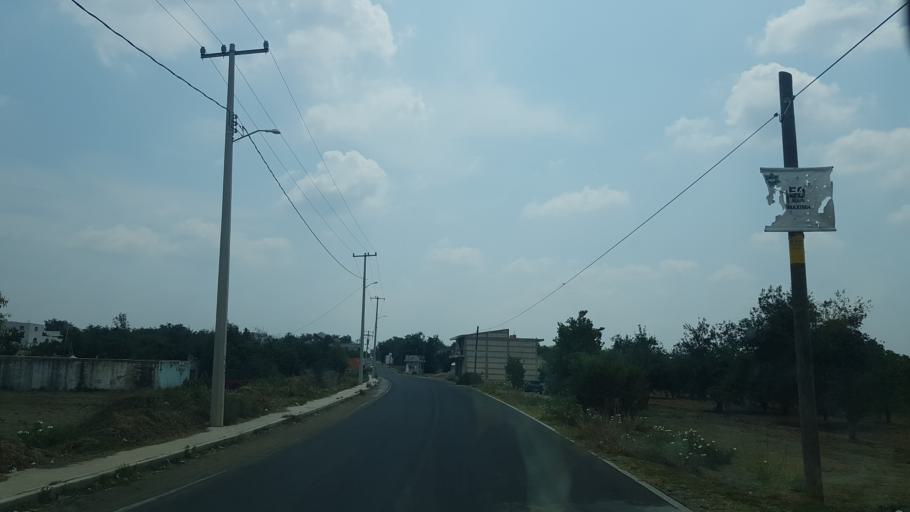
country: MX
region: Puebla
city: Domingo Arenas
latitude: 19.1412
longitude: -98.4708
